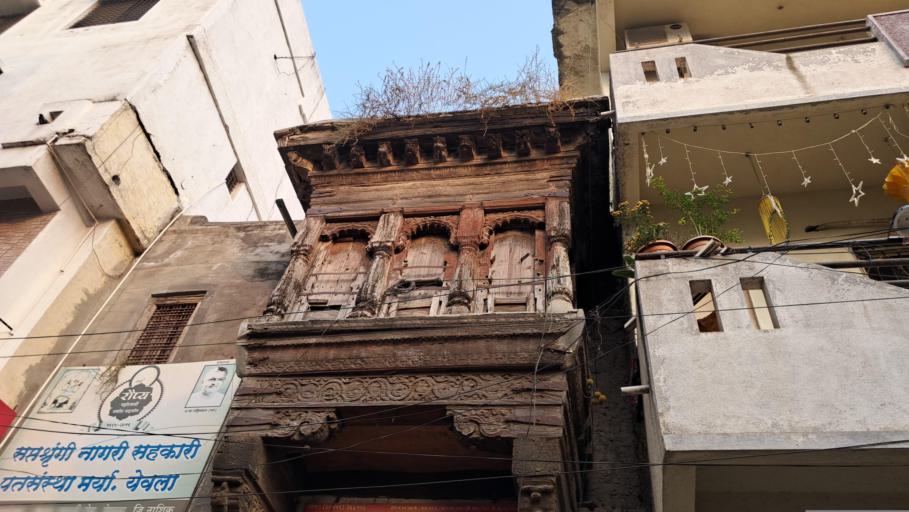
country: IN
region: Maharashtra
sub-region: Nashik Division
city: Yeola
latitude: 20.0408
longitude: 74.4900
